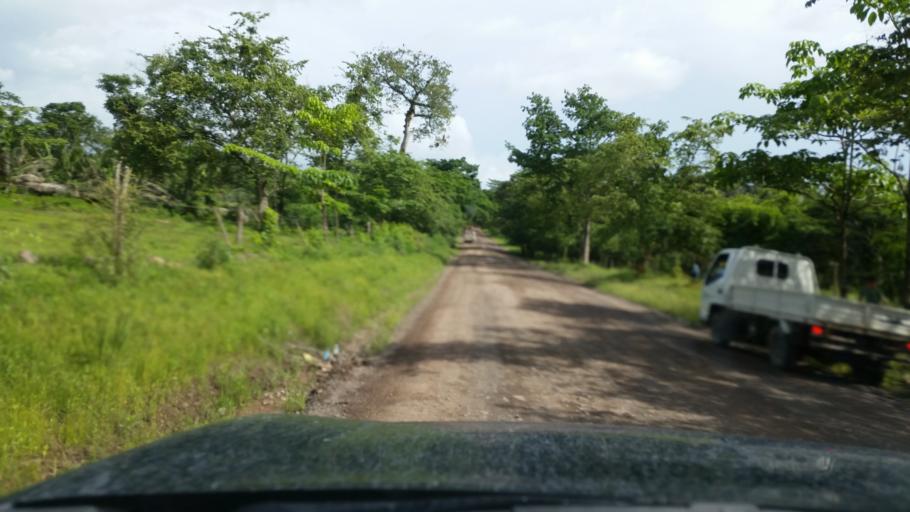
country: NI
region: Atlantico Norte (RAAN)
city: Siuna
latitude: 13.6863
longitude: -84.7898
